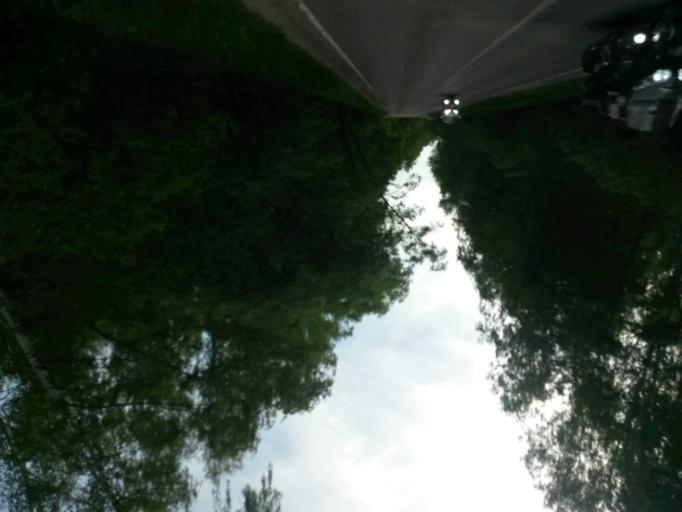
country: RU
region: Moskovskaya
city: Melikhovo
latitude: 55.2141
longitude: 37.6880
